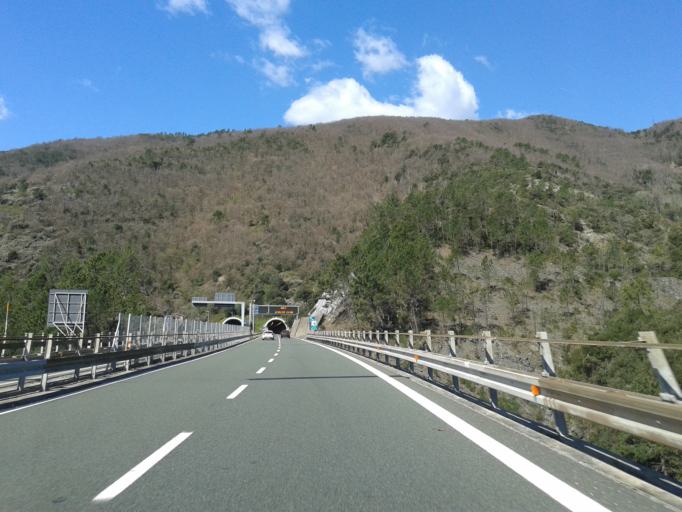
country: IT
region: Liguria
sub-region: Provincia di La Spezia
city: Deiva Marina
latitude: 44.2451
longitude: 9.5421
